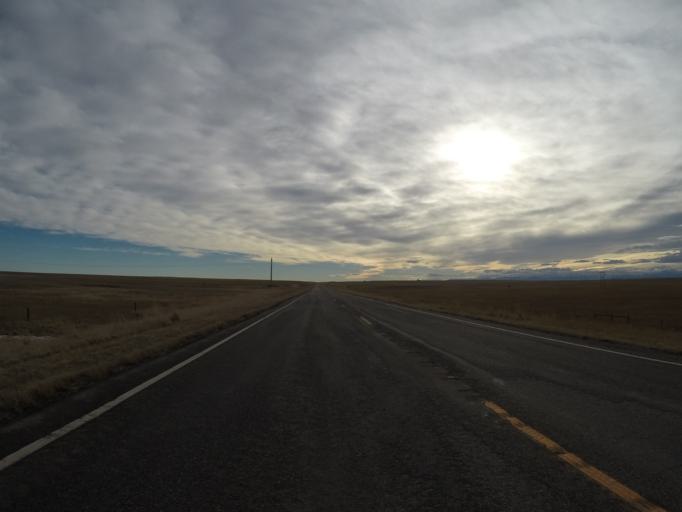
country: US
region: Montana
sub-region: Yellowstone County
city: Laurel
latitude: 45.8513
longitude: -108.8812
